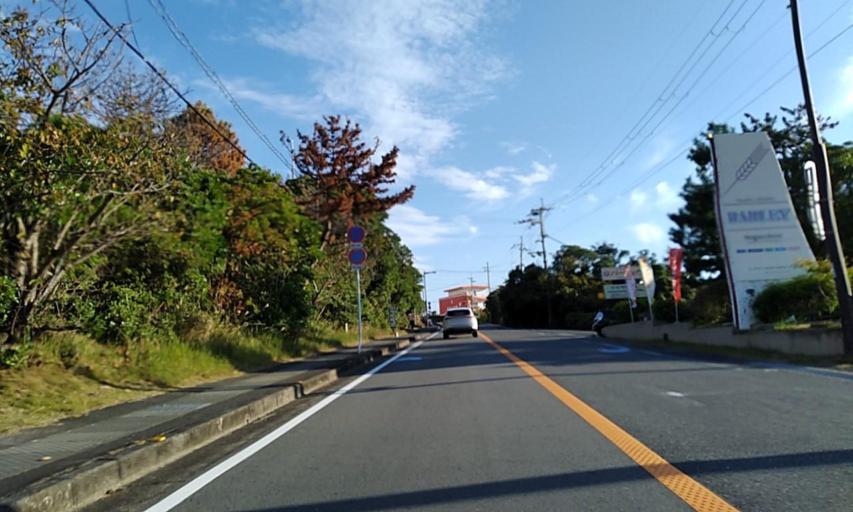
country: JP
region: Wakayama
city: Tanabe
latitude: 33.6695
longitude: 135.3339
